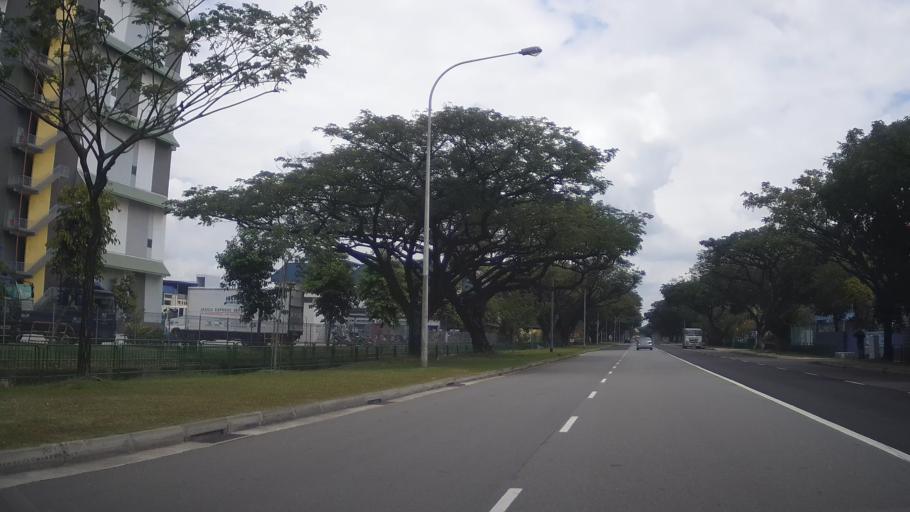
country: MY
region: Johor
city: Johor Bahru
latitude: 1.3129
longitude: 103.6707
